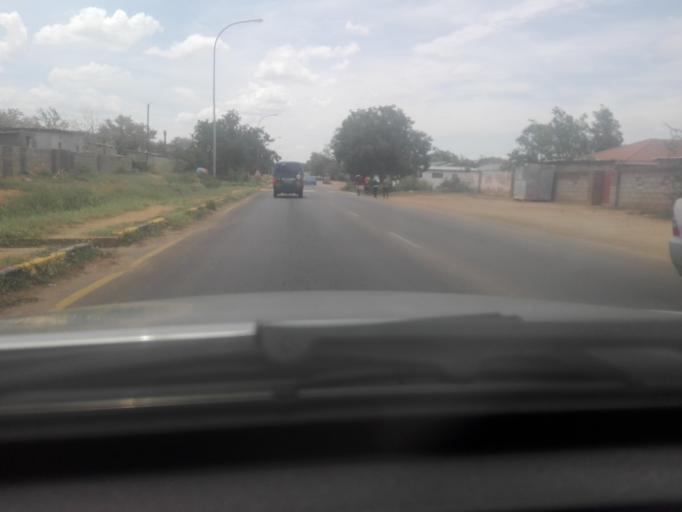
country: BW
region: South East
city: Gaborone
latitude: -24.6244
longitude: 25.9434
